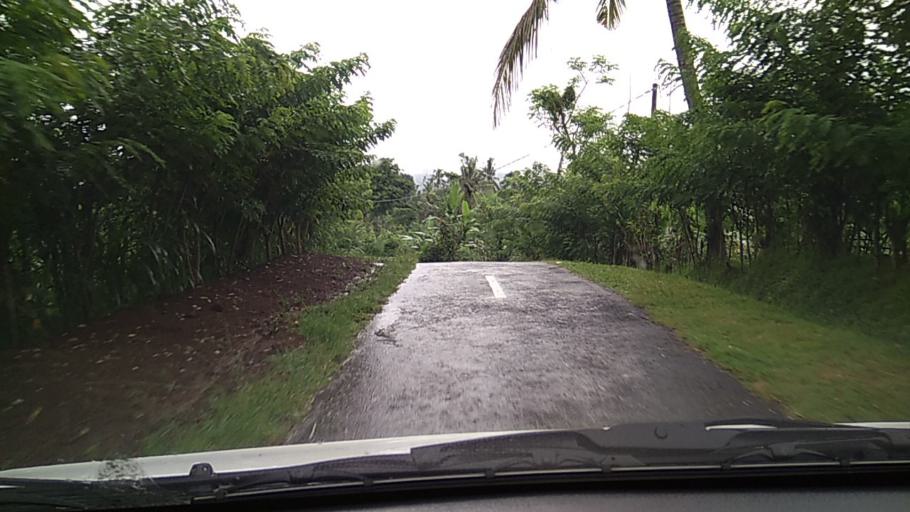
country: ID
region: Bali
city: Tiyingtali Kelod
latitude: -8.4031
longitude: 115.6295
